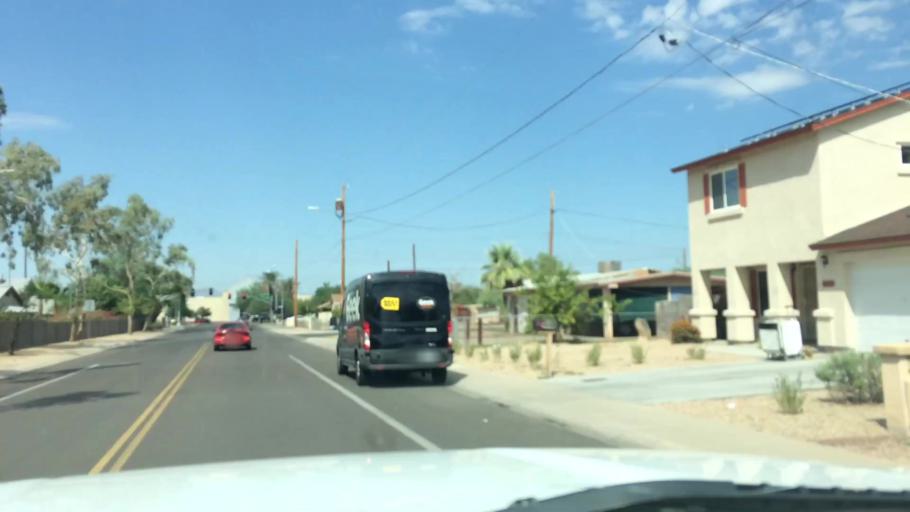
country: US
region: Arizona
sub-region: Maricopa County
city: Peoria
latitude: 33.5772
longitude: -112.2532
